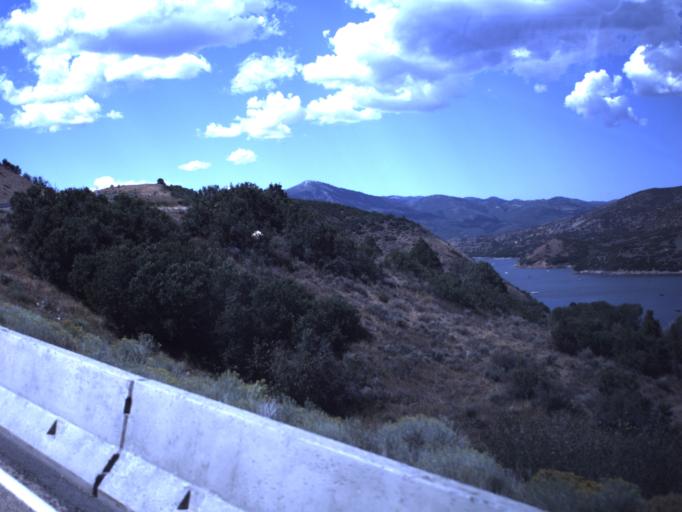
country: US
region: Utah
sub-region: Summit County
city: Francis
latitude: 40.5982
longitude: -111.3429
